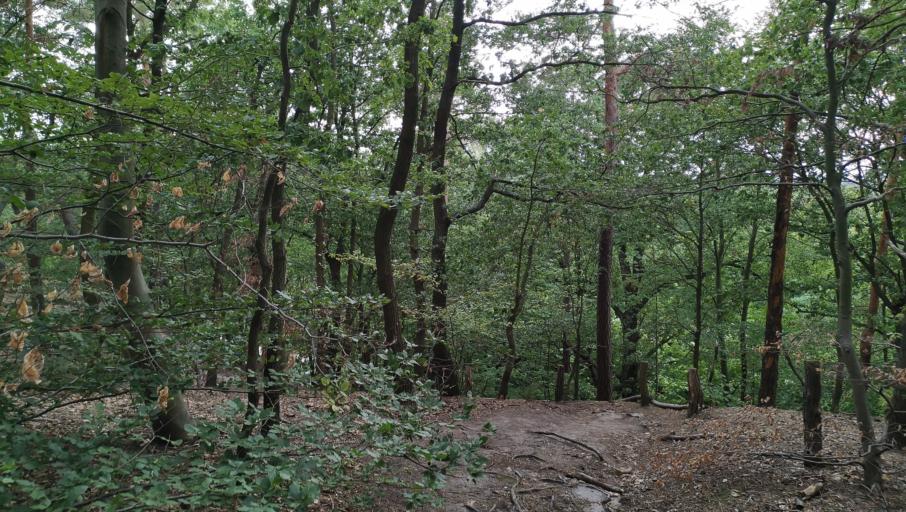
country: DE
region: Brandenburg
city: Potsdam
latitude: 52.3665
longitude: 13.0306
